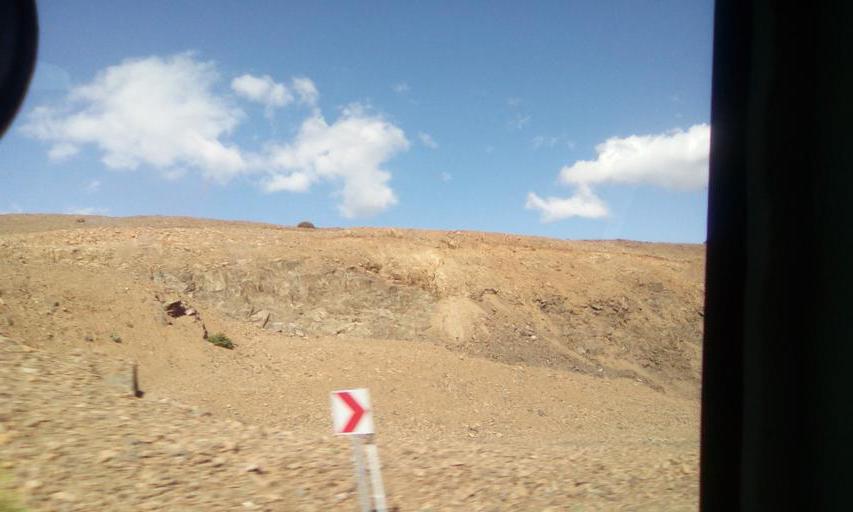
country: LS
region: Qacha's Nek
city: Qacha's Nek
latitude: -30.0456
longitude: 28.2765
